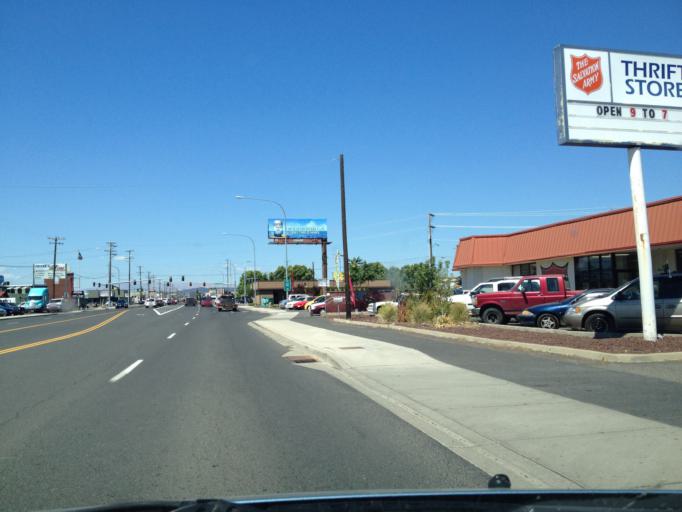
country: US
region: Washington
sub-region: Yakima County
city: Union Gap
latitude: 46.5617
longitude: -120.4779
